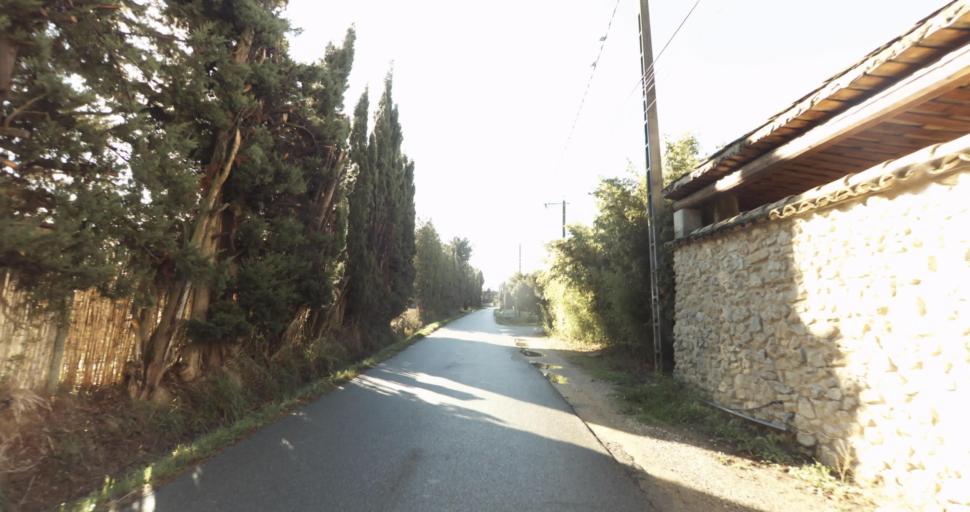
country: FR
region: Provence-Alpes-Cote d'Azur
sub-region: Departement des Bouches-du-Rhone
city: Rognonas
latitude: 43.8904
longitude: 4.8029
